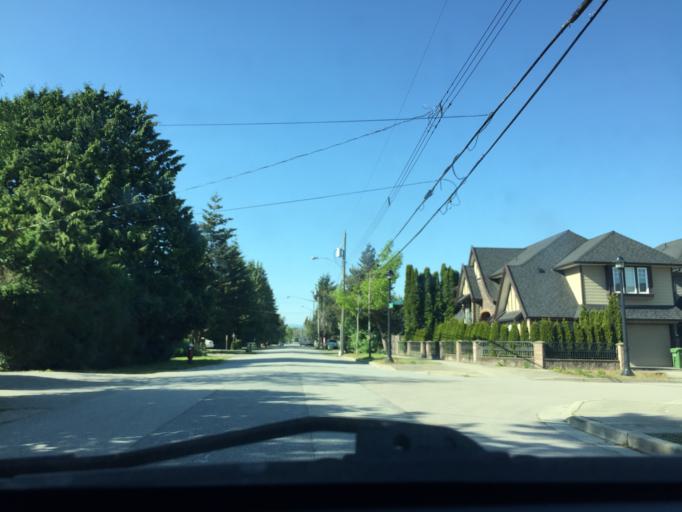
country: CA
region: British Columbia
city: Richmond
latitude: 49.1566
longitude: -123.1198
